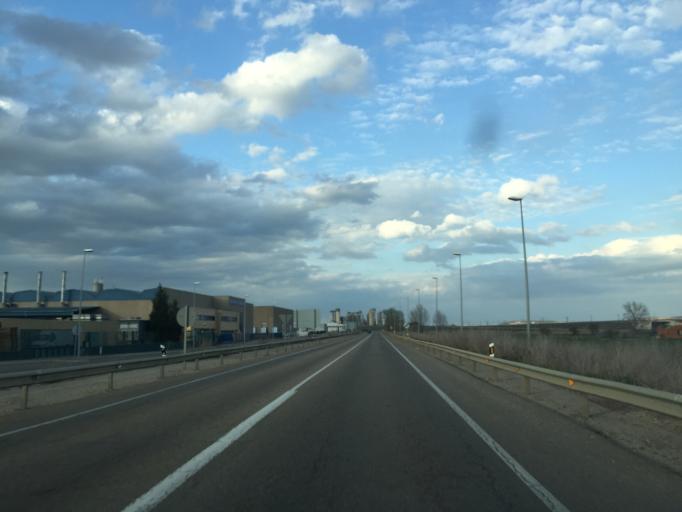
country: ES
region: Castille and Leon
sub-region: Provincia de Palencia
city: Venta de Banos
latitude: 41.9310
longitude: -4.4829
